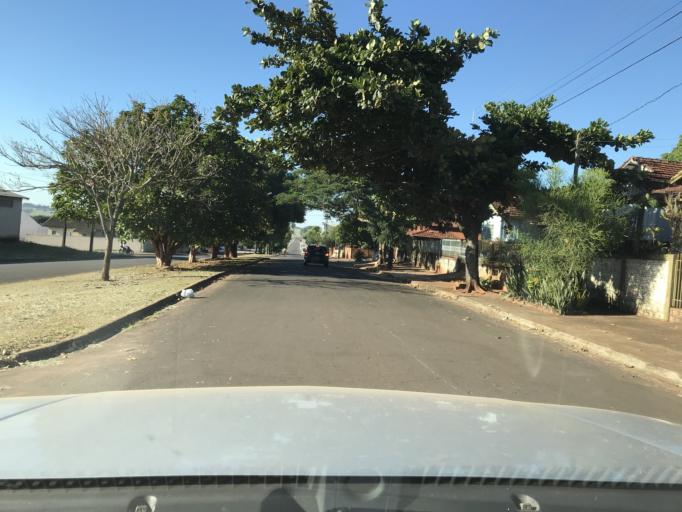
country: BR
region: Parana
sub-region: Ipora
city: Ipora
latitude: -23.9975
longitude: -53.7051
